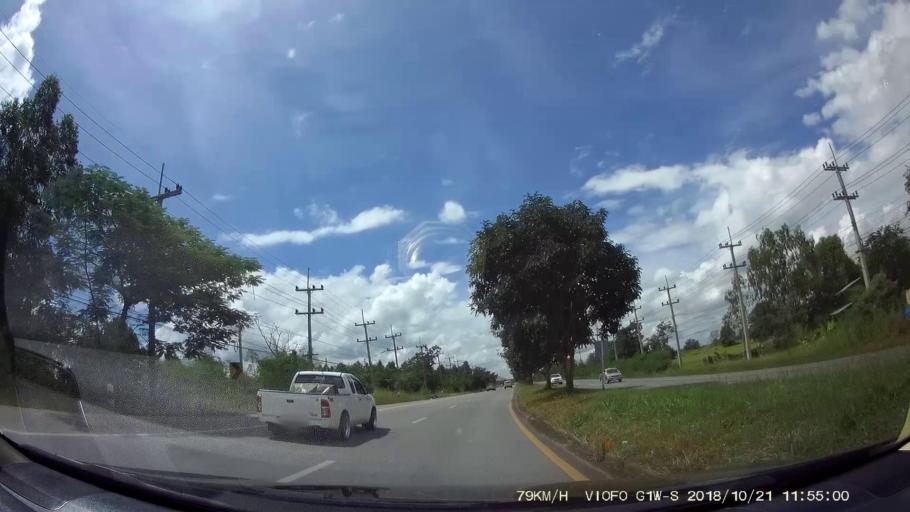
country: TH
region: Chaiyaphum
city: Chatturat
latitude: 15.5793
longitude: 101.8968
